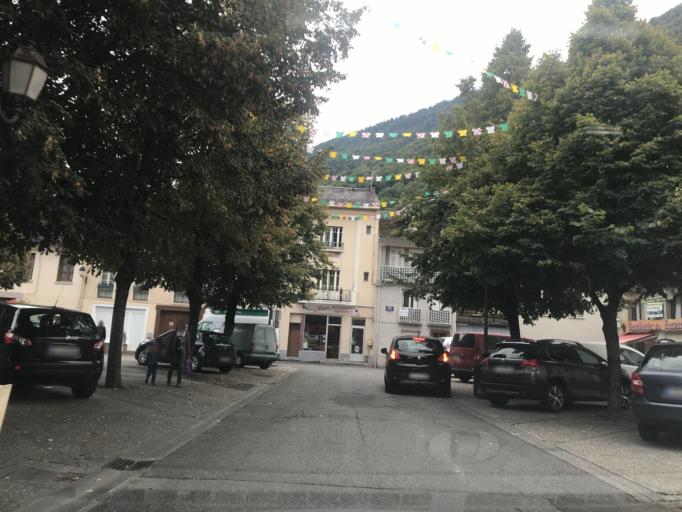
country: FR
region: Midi-Pyrenees
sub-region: Departement de la Haute-Garonne
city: Bagneres-de-Luchon
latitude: 42.7913
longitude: 0.5890
